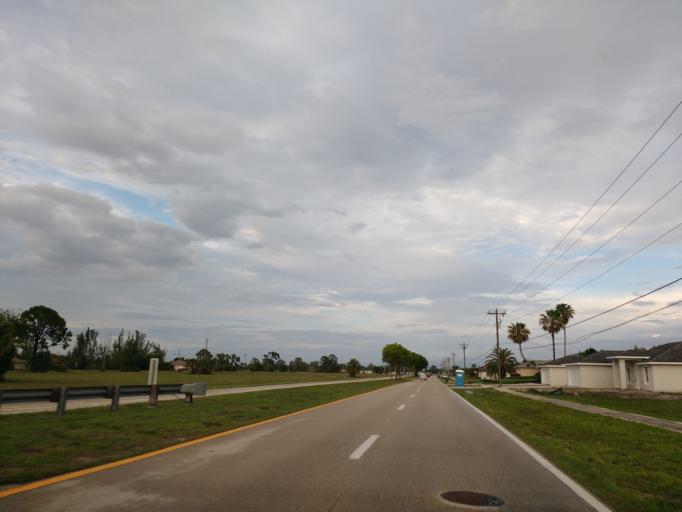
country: US
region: Florida
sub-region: Lee County
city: Cape Coral
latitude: 26.6227
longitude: -81.9965
